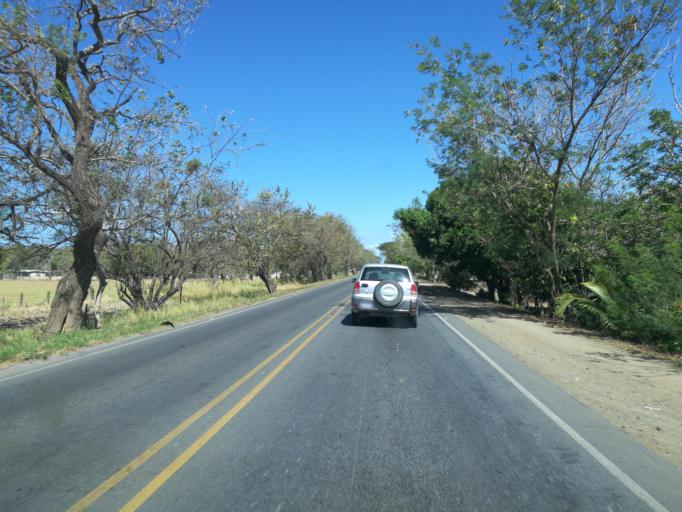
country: CR
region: Guanacaste
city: Liberia
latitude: 10.6541
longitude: -85.4662
